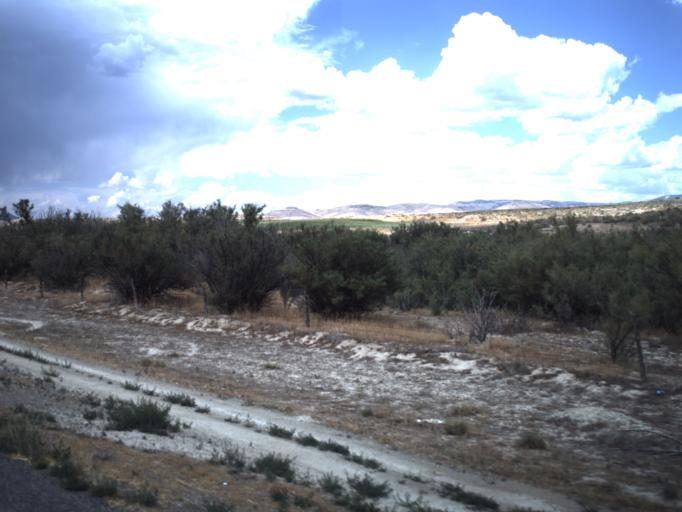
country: US
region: Utah
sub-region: Sanpete County
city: Centerfield
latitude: 39.1387
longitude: -111.7839
